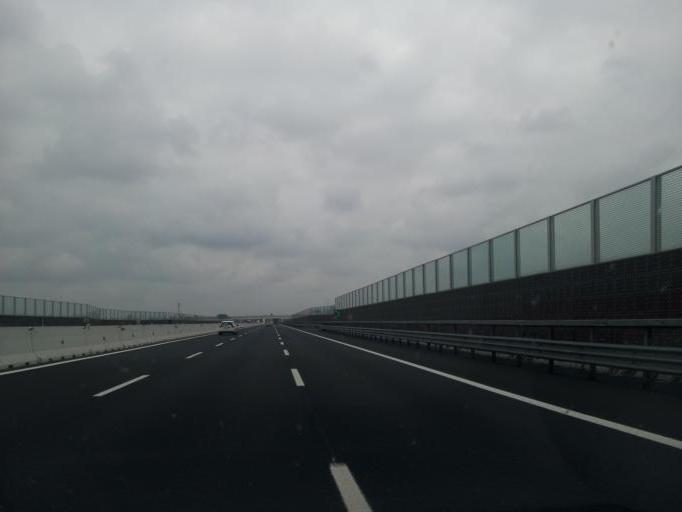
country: IT
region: Veneto
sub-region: Provincia di Venezia
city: Fossalta di Piave
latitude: 45.6563
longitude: 12.4967
